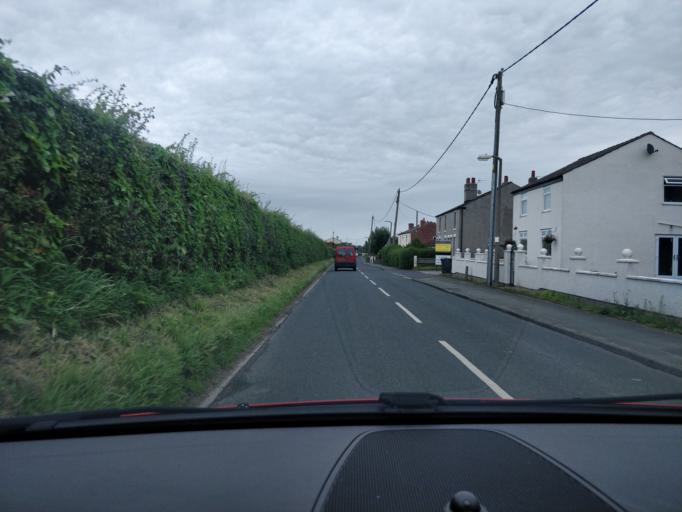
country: GB
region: England
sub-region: Lancashire
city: Ormskirk
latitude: 53.6049
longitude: -2.8648
